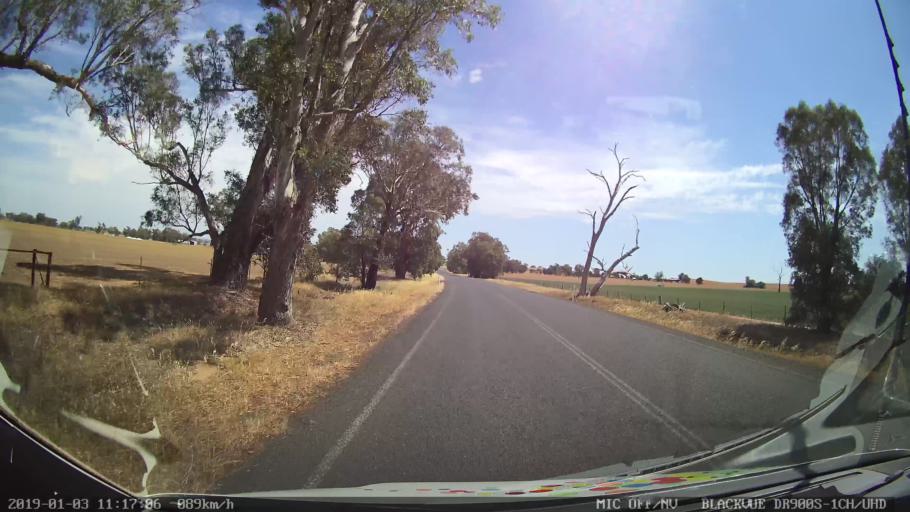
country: AU
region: New South Wales
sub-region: Young
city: Young
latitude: -34.1430
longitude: 148.2674
